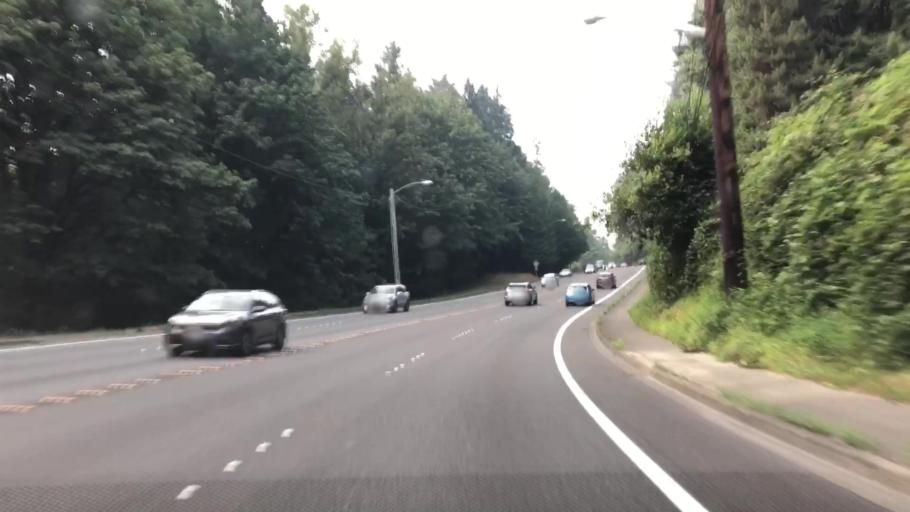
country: US
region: Washington
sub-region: King County
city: Newport
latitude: 47.5599
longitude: -122.1691
